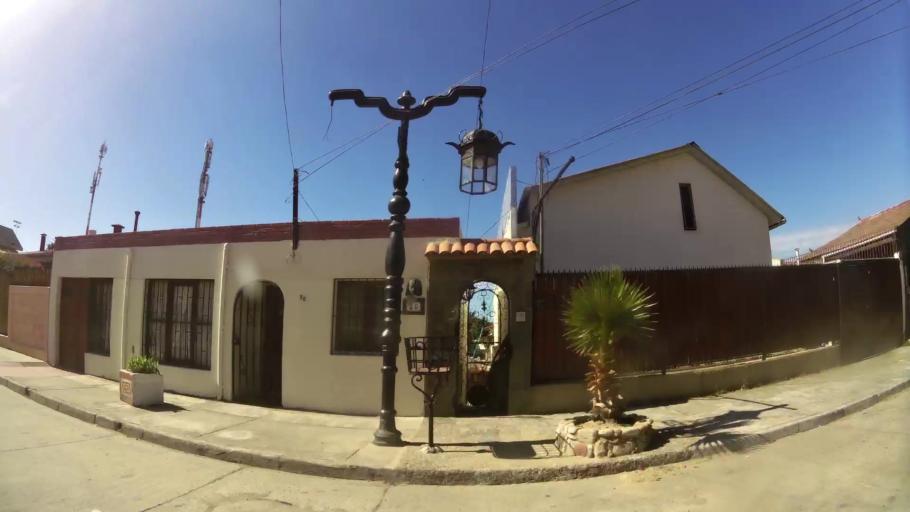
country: CL
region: Valparaiso
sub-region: Provincia de Valparaiso
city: Vina del Mar
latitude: -33.0333
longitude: -71.5691
